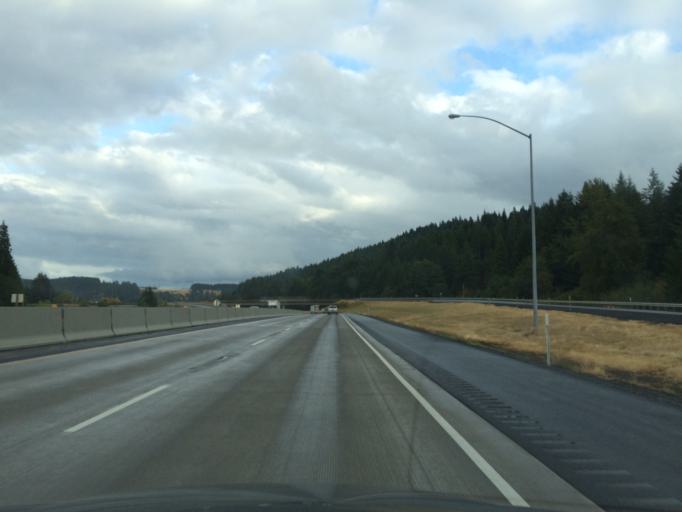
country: US
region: Oregon
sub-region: Lane County
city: Cottage Grove
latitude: 43.7513
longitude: -123.1287
